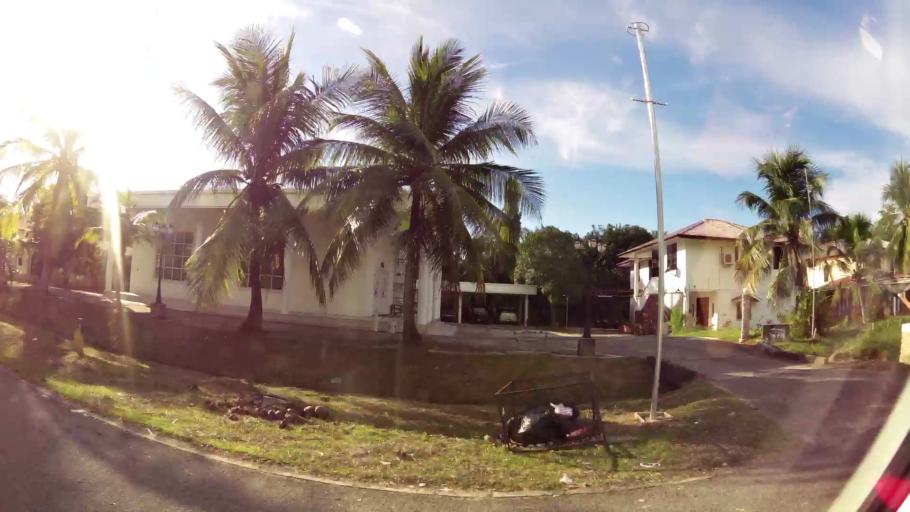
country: BN
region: Brunei and Muara
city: Bandar Seri Begawan
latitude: 4.9881
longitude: 114.9749
